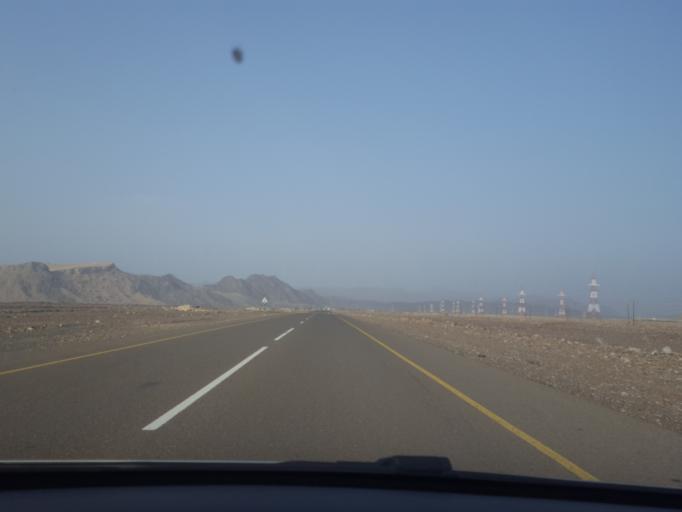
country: AE
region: Abu Dhabi
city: Al Ain
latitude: 24.0428
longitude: 56.0302
